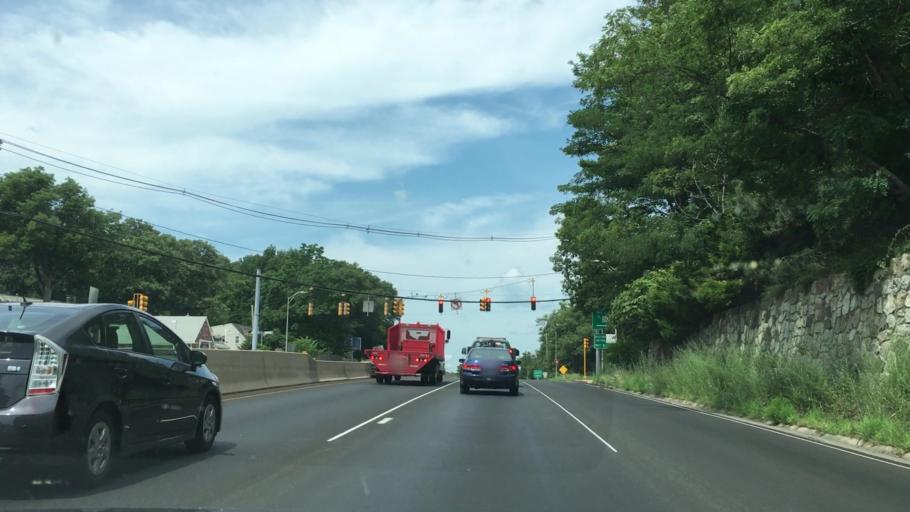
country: US
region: Massachusetts
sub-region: Middlesex County
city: Lincoln
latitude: 42.4404
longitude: -71.2981
